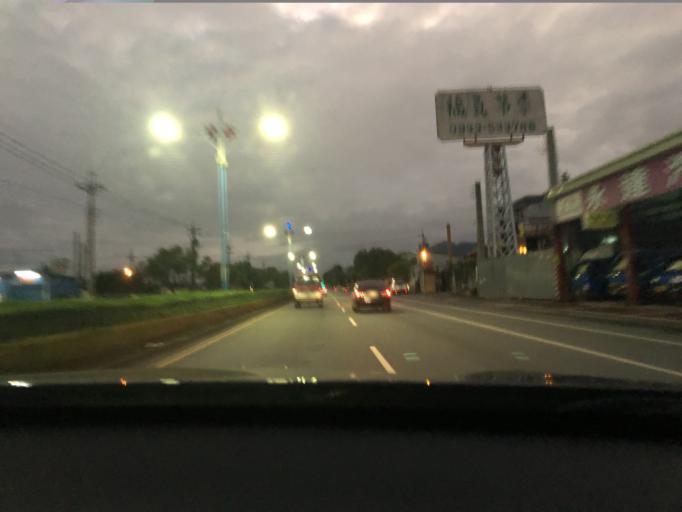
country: TW
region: Taiwan
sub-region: Hualien
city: Hualian
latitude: 23.9638
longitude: 121.5664
